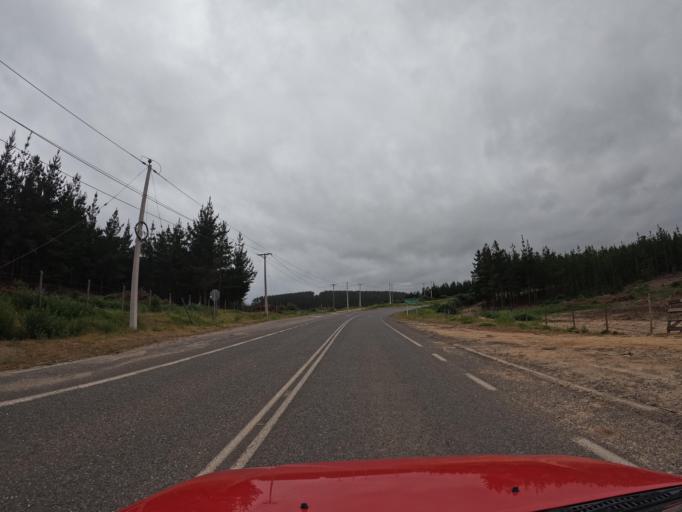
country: CL
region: O'Higgins
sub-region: Provincia de Colchagua
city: Santa Cruz
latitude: -34.6365
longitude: -72.0357
